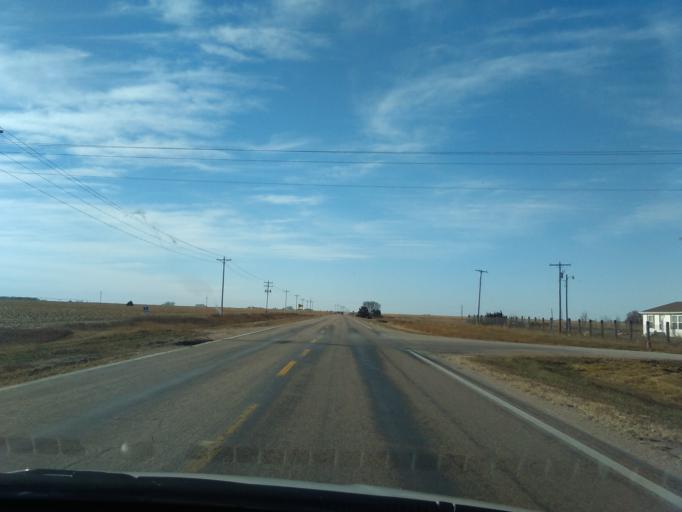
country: US
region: Nebraska
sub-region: Clay County
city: Harvard
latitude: 40.6115
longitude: -98.1023
